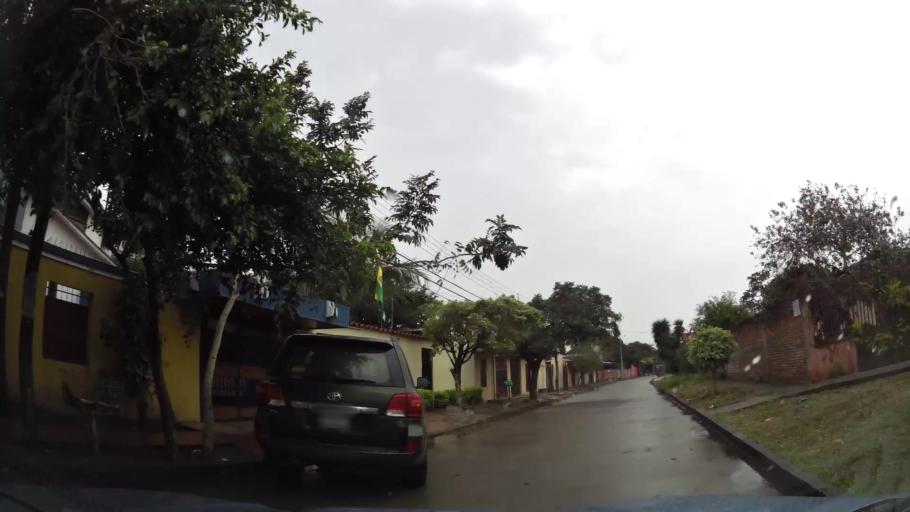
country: BO
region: Santa Cruz
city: Santa Cruz de la Sierra
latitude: -17.7689
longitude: -63.1488
